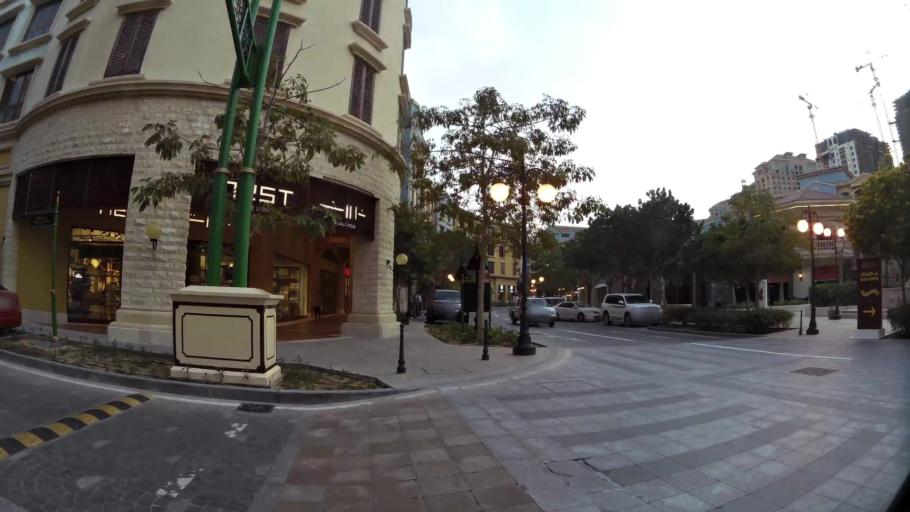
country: QA
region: Baladiyat ad Dawhah
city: Doha
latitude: 25.3681
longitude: 51.5515
